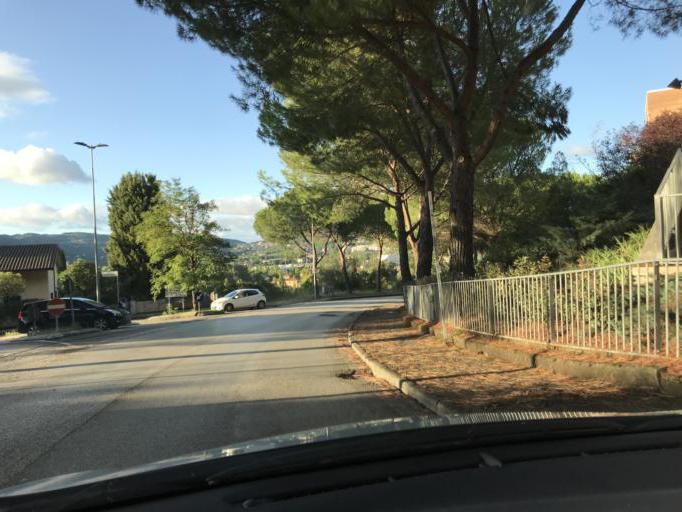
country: IT
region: Umbria
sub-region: Provincia di Perugia
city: Perugia
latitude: 43.0999
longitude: 12.3625
